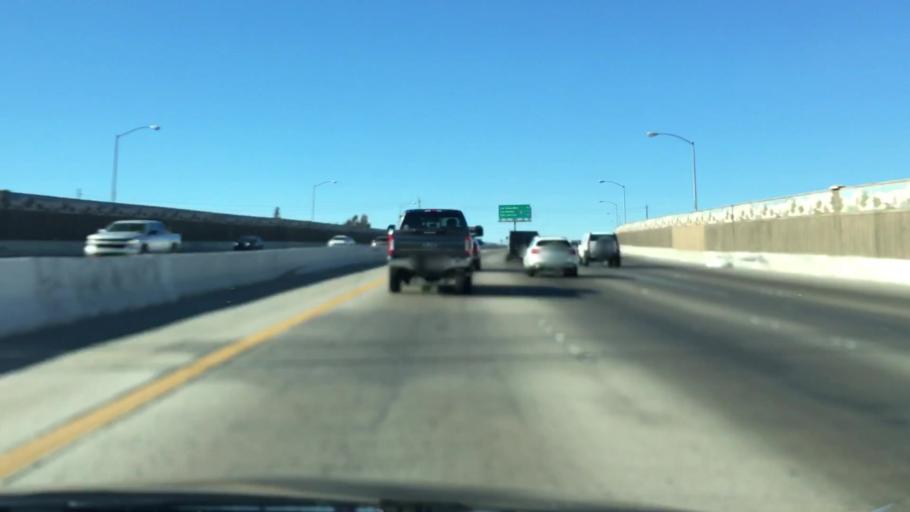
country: US
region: Nevada
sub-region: Clark County
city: Las Vegas
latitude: 36.1684
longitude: -115.1255
